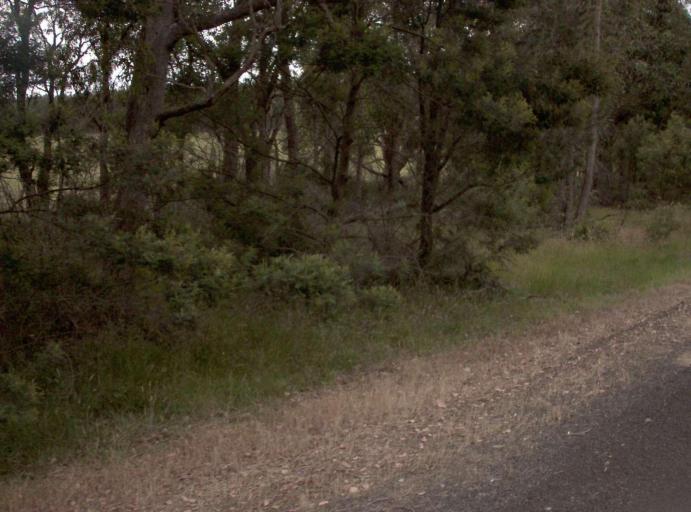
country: AU
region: Victoria
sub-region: Wellington
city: Sale
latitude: -38.3504
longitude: 146.9984
